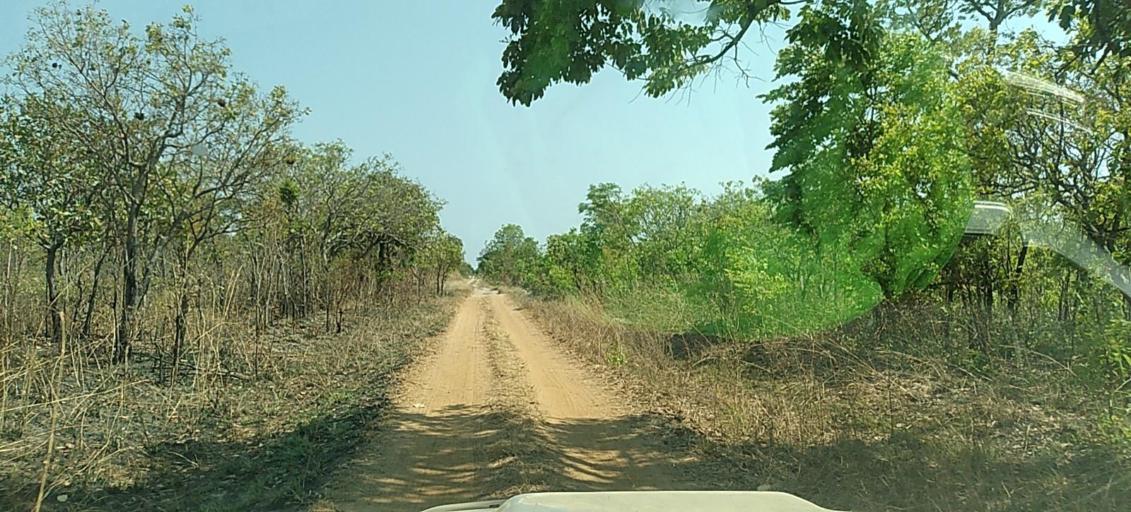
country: ZM
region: North-Western
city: Kalengwa
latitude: -13.2448
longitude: 24.7586
